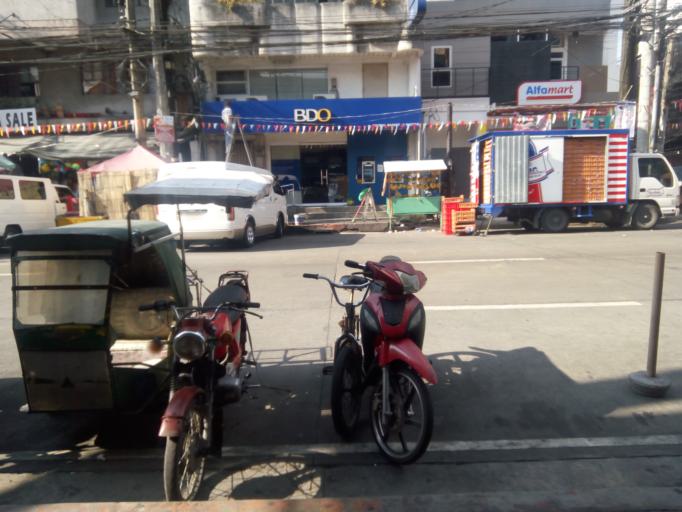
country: PH
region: Metro Manila
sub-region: City of Manila
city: Manila
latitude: 14.6083
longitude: 120.9845
